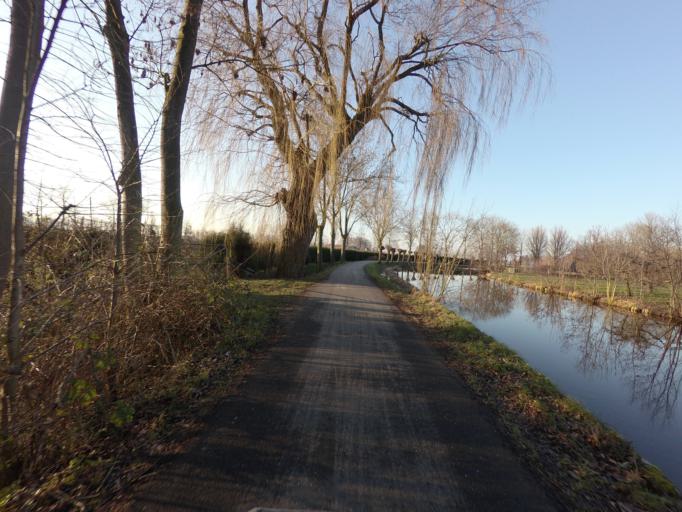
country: NL
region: South Holland
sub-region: Gemeente Giessenlanden
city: Giessenburg
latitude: 51.8957
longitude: 4.9310
